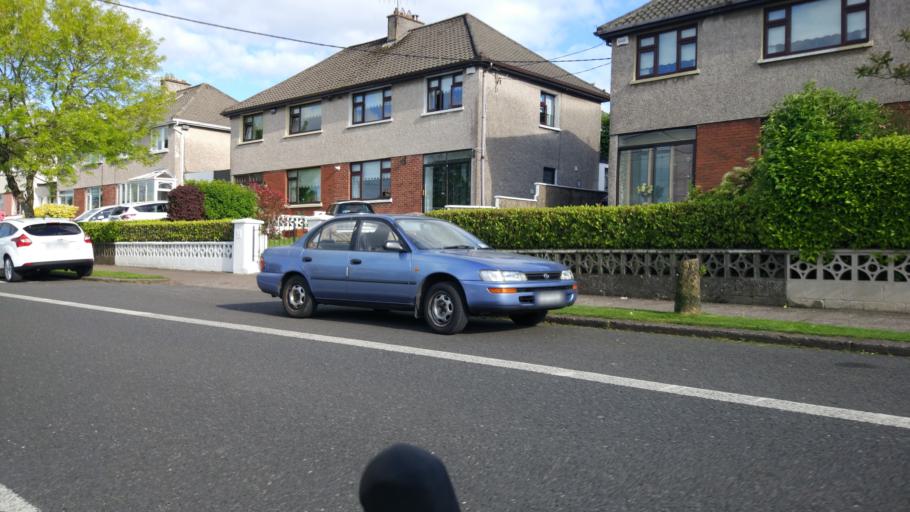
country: IE
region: Munster
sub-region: County Cork
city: Cork
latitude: 51.9107
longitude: -8.4467
